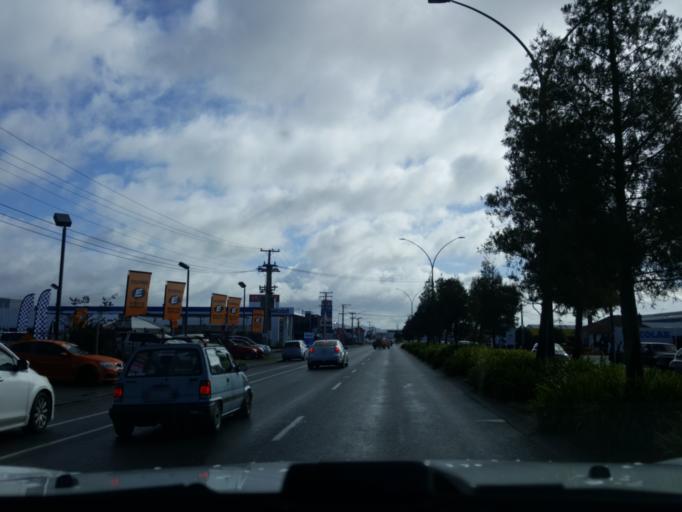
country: NZ
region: Waikato
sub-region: Hamilton City
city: Hamilton
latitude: -37.7565
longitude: 175.2447
